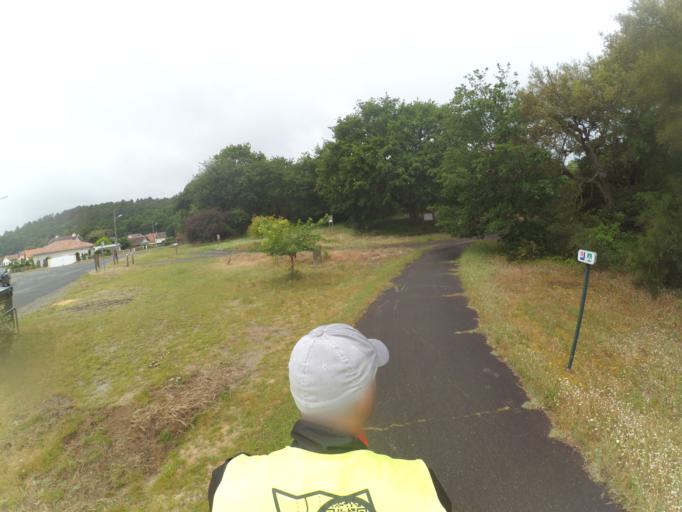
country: FR
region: Aquitaine
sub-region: Departement des Landes
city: Mimizan
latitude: 44.2174
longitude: -1.2347
